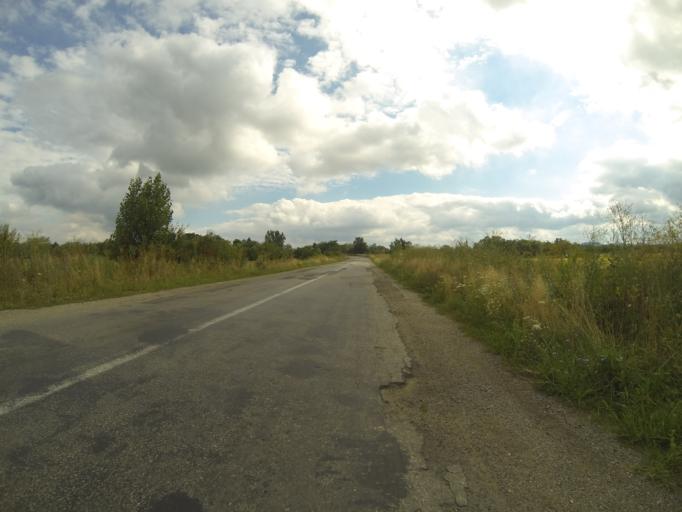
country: RO
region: Brasov
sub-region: Comuna Sinca Veche
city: Sinca Veche
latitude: 45.7879
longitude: 25.1485
